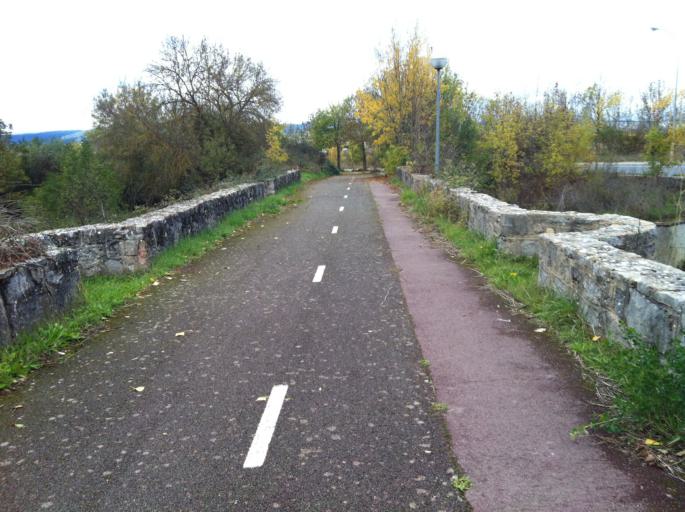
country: ES
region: Basque Country
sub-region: Provincia de Alava
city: Gasteiz / Vitoria
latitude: 42.8583
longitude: -2.7231
